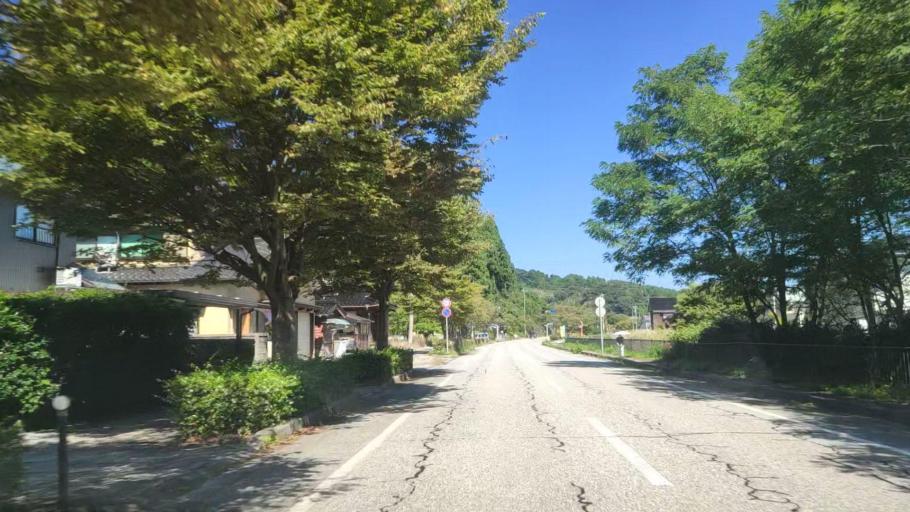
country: JP
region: Ishikawa
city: Nanao
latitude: 37.3905
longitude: 136.8926
